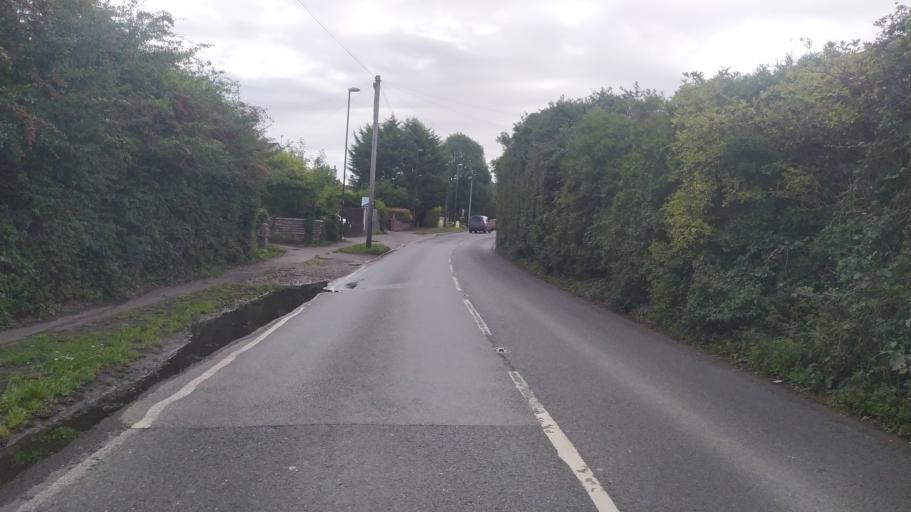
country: GB
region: England
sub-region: West Sussex
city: Chichester
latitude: 50.8150
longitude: -0.7527
